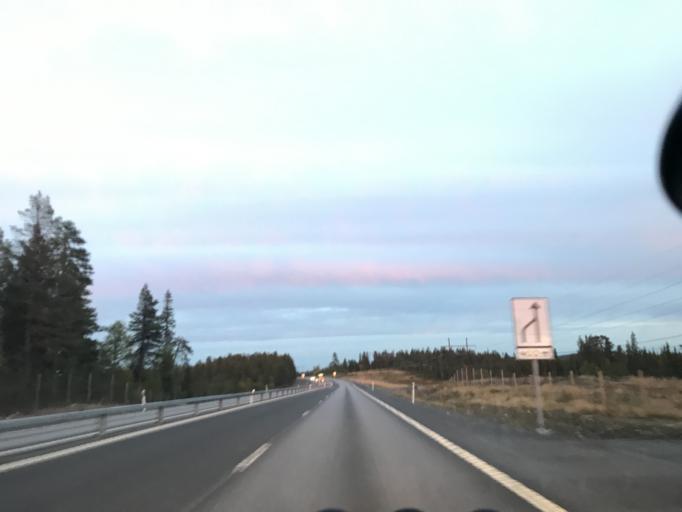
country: SE
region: Norrbotten
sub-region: Gallivare Kommun
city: Malmberget
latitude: 67.6740
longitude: 20.9067
